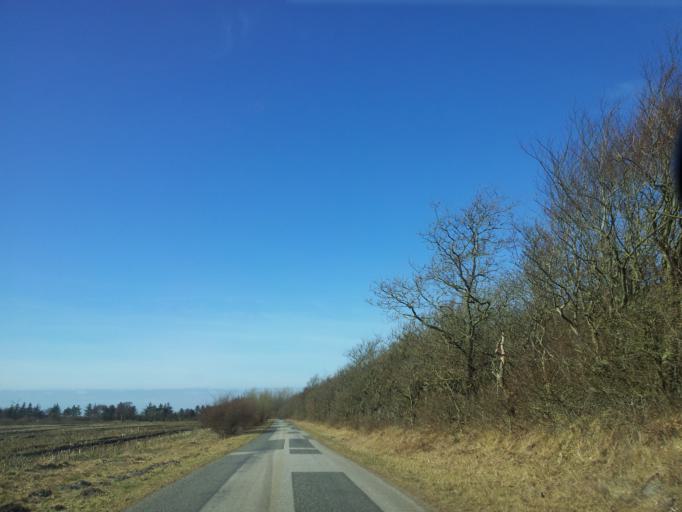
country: DK
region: South Denmark
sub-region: Tonder Kommune
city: Sherrebek
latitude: 55.2053
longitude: 8.7412
